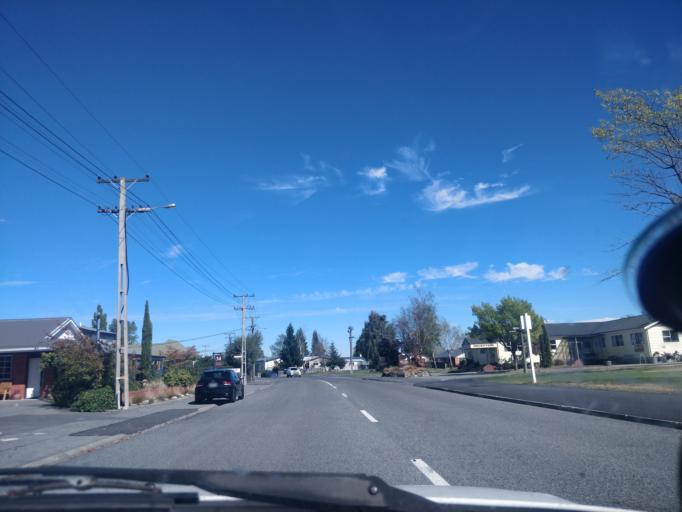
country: NZ
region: Canterbury
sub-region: Timaru District
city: Pleasant Point
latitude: -44.2588
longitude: 170.0989
